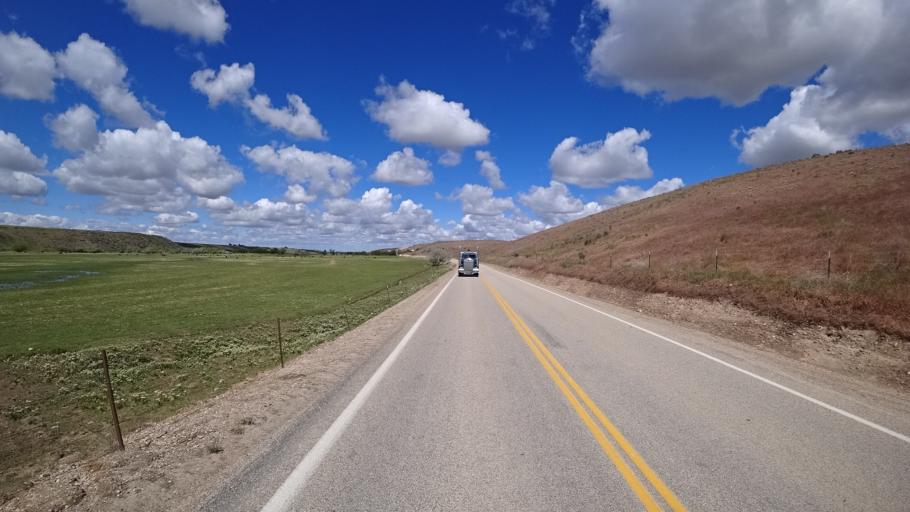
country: US
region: Idaho
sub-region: Ada County
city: Garden City
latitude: 43.4950
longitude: -116.2777
